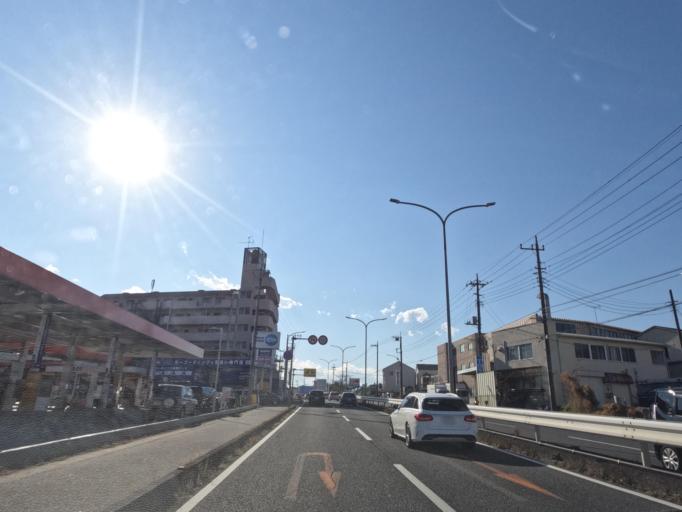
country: JP
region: Saitama
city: Wako
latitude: 35.7890
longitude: 139.6278
